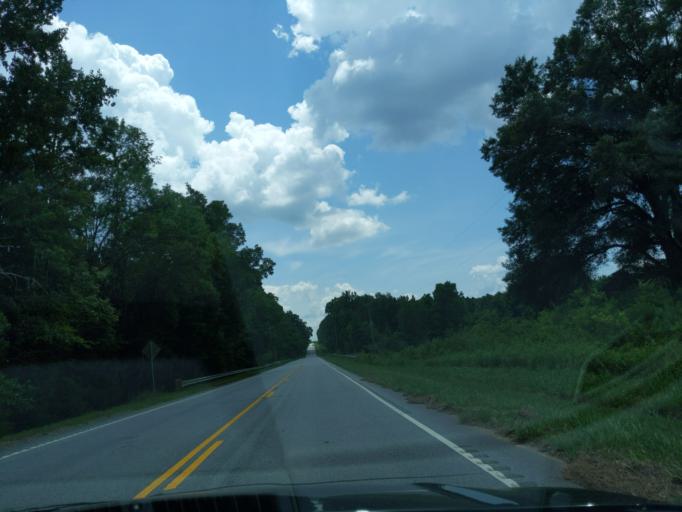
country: US
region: South Carolina
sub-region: Greenwood County
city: Ninety Six
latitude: 34.0270
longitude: -82.0402
